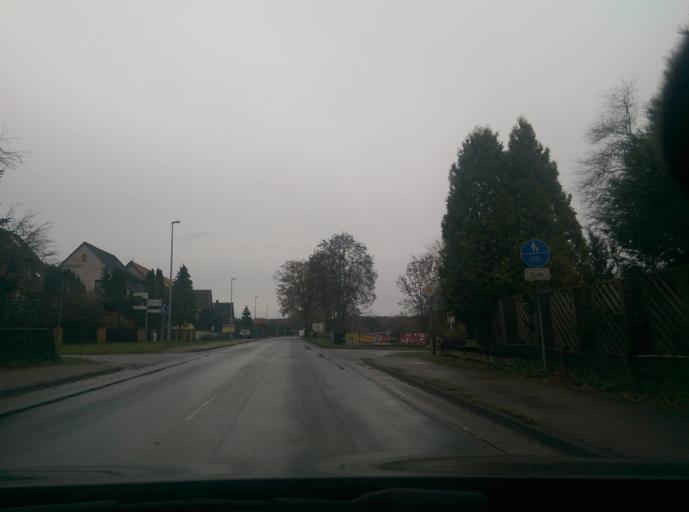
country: DE
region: Lower Saxony
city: Lindwedel
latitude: 52.5684
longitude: 9.6147
